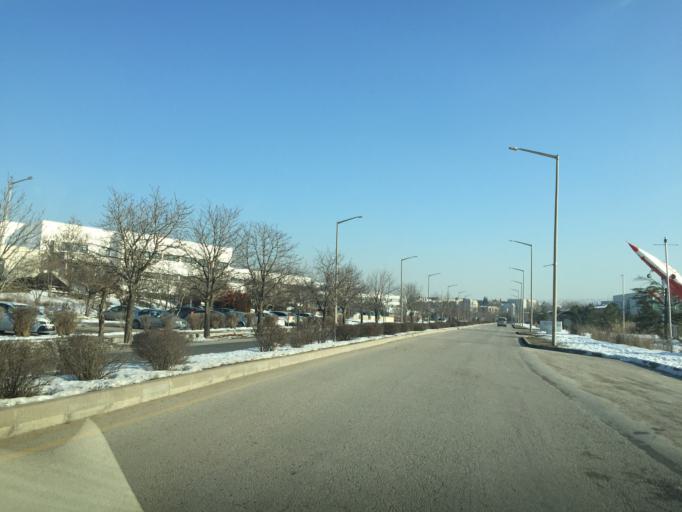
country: TR
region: Ankara
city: Batikent
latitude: 39.9019
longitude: 32.7721
